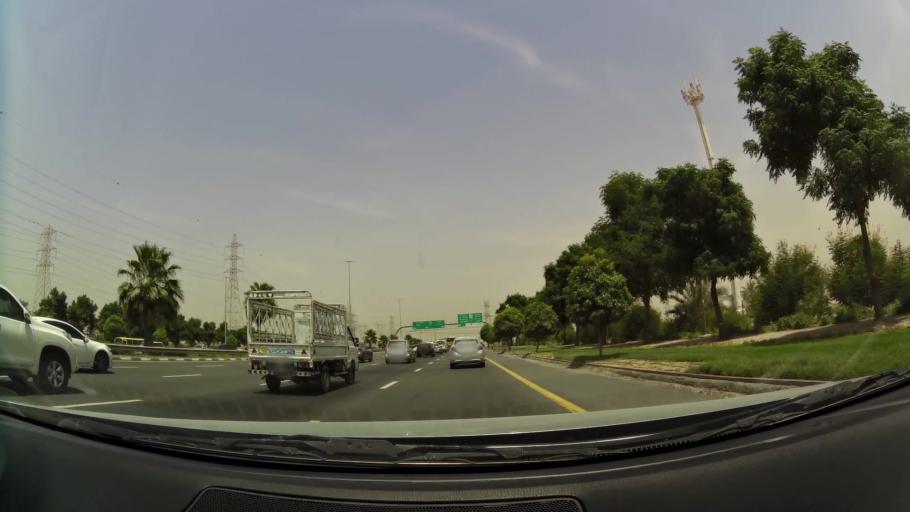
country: AE
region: Ash Shariqah
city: Sharjah
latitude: 25.2123
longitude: 55.3952
